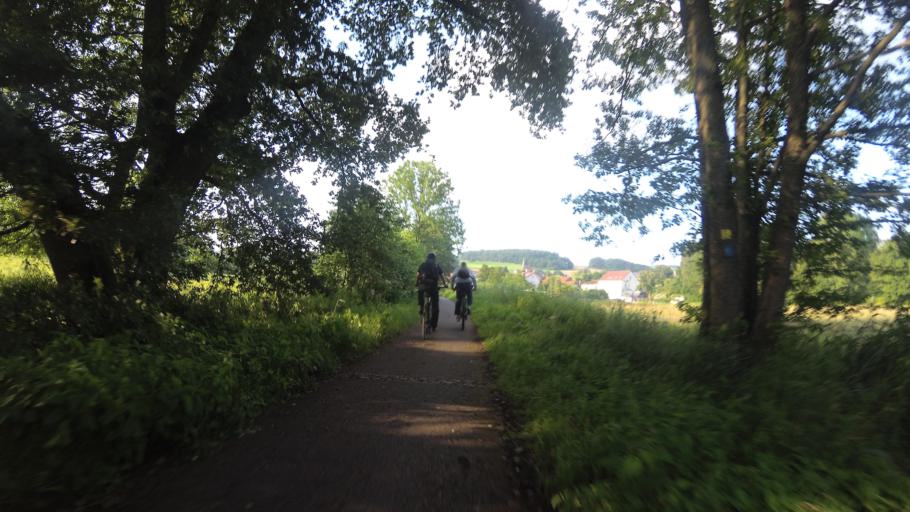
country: DE
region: Rheinland-Pfalz
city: Althornbach
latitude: 49.2006
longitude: 7.3736
